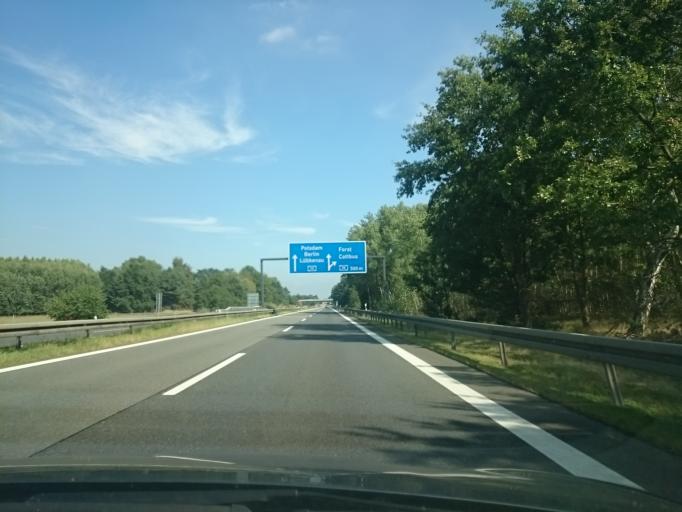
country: DE
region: Brandenburg
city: Lubbenau
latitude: 51.8353
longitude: 13.9160
